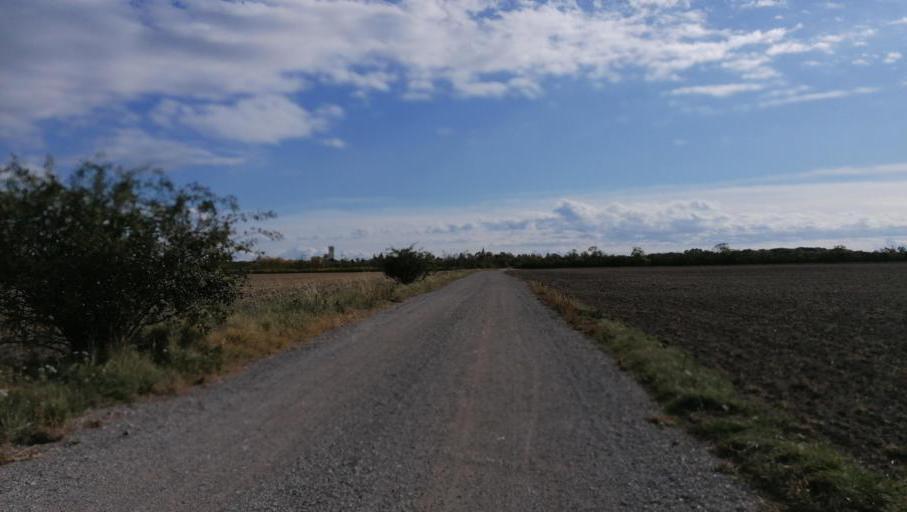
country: AT
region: Lower Austria
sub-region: Politischer Bezirk Baden
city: Teesdorf
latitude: 47.9665
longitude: 16.2912
